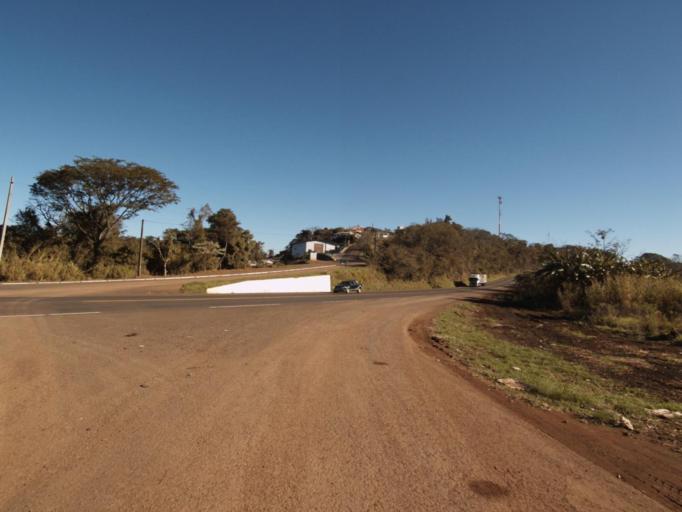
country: BR
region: Santa Catarina
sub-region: Chapeco
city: Chapeco
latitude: -26.9825
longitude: -52.5983
